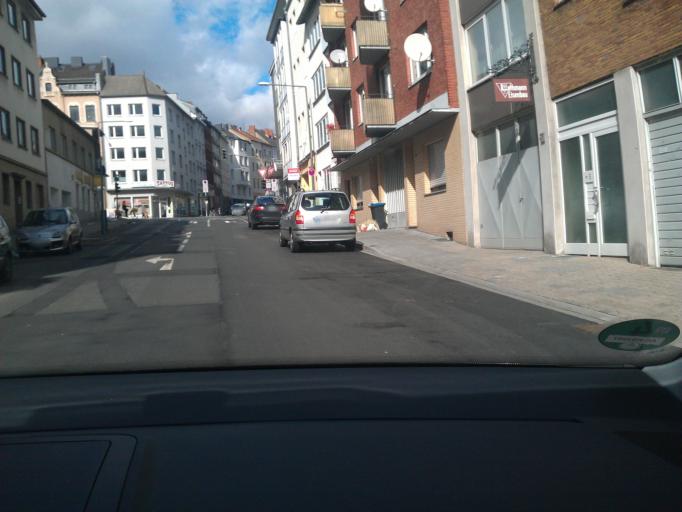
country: DE
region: North Rhine-Westphalia
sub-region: Regierungsbezirk Koln
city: Aachen
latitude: 50.7783
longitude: 6.0991
